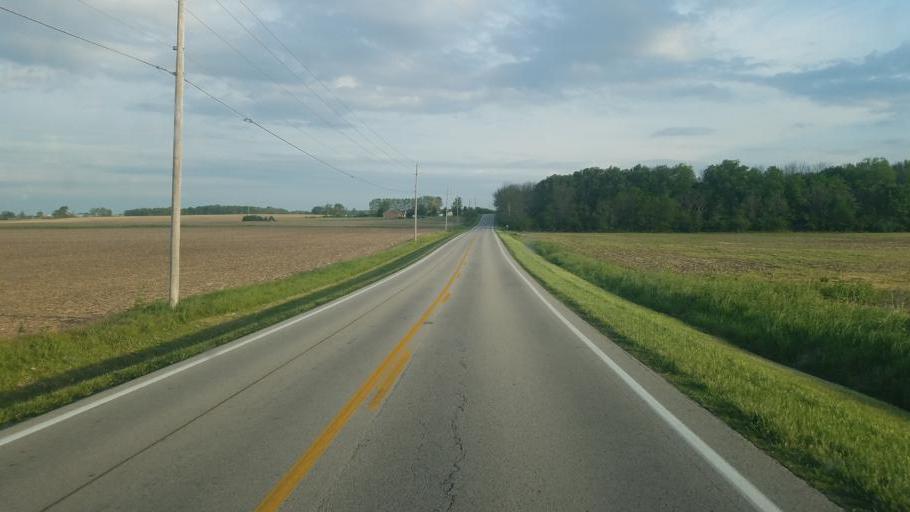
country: US
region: Ohio
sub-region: Clinton County
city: Sabina
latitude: 39.4610
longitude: -83.6591
